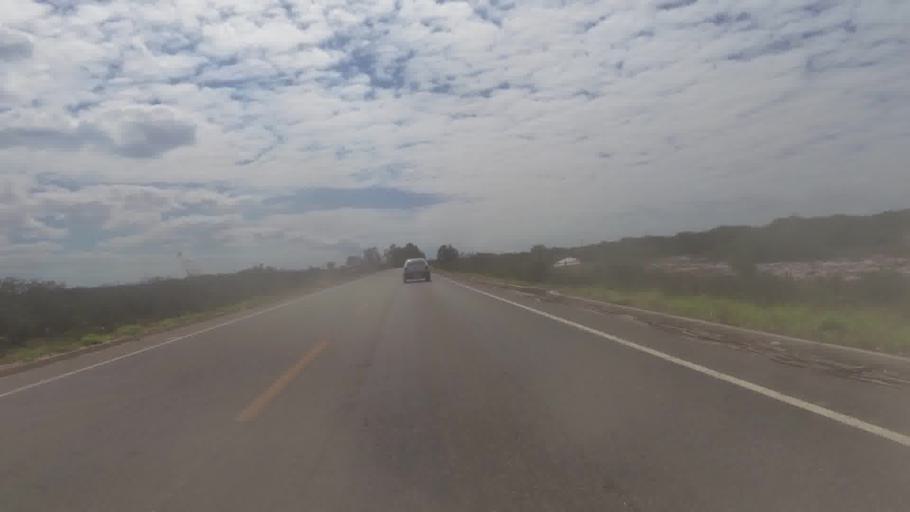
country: BR
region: Espirito Santo
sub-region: Marataizes
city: Marataizes
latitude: -21.2269
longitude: -40.9729
